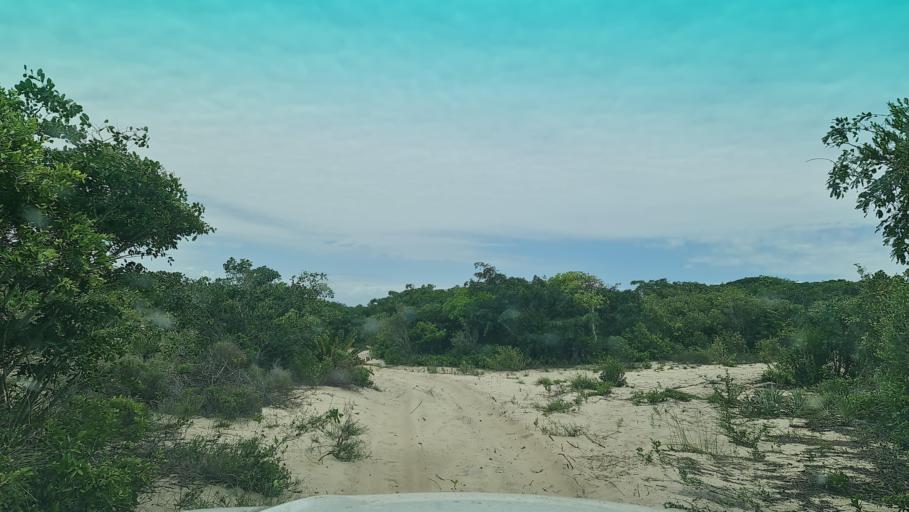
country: MZ
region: Maputo
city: Manhica
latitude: -25.6374
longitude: 32.7840
